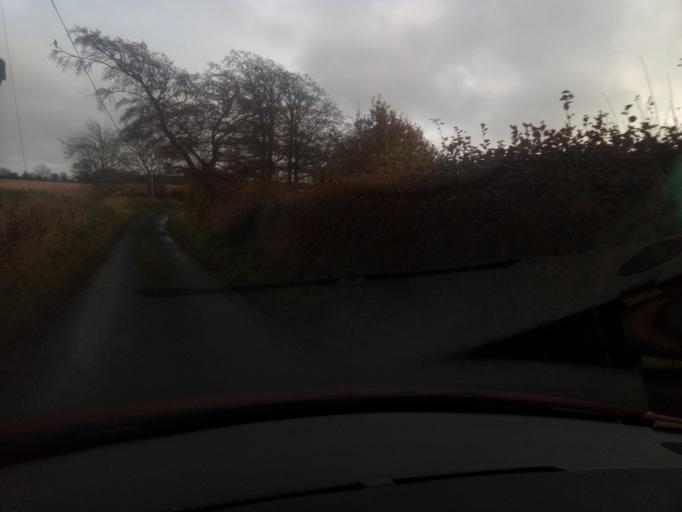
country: GB
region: Scotland
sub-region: The Scottish Borders
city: Jedburgh
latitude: 55.4872
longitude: -2.6135
